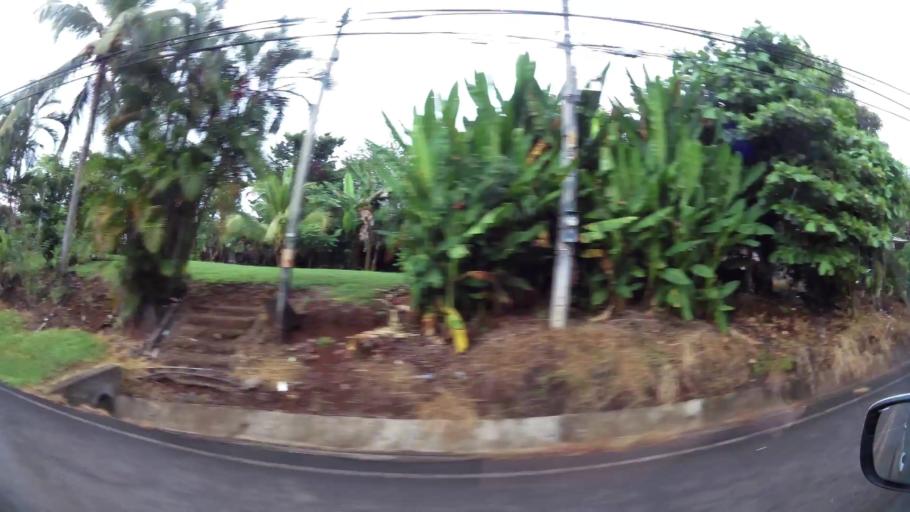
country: CR
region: Puntarenas
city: Esparza
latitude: 9.9790
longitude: -84.6215
